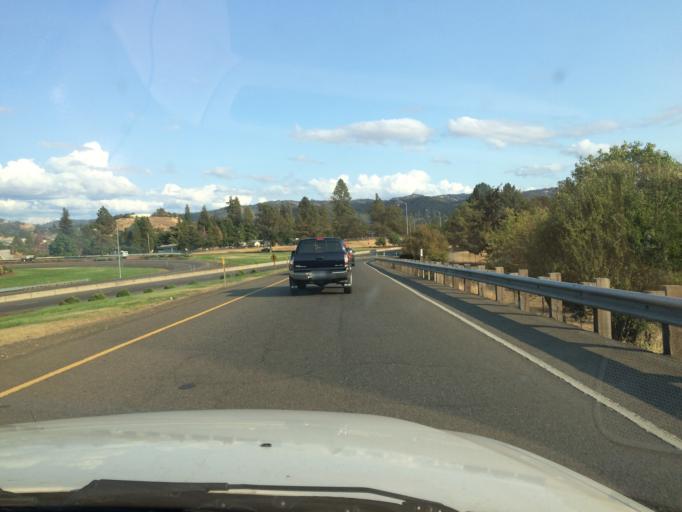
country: US
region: Oregon
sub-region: Douglas County
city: Roseburg
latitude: 43.2268
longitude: -123.3620
